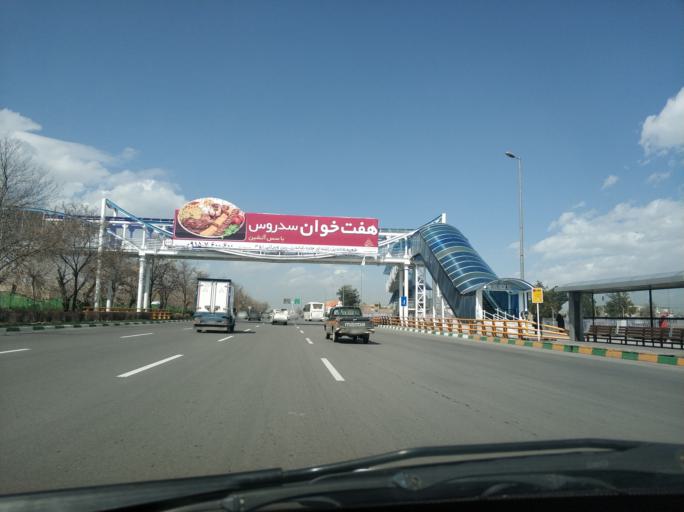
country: IR
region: Razavi Khorasan
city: Torqabeh
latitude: 36.3411
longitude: 59.4586
